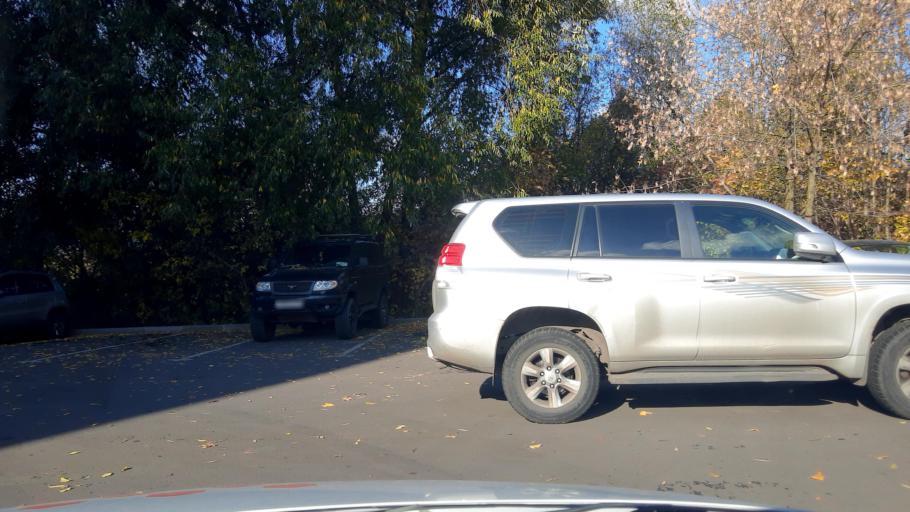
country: RU
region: Moscow
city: Orekhovo-Borisovo Severnoye
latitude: 55.6252
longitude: 37.7038
